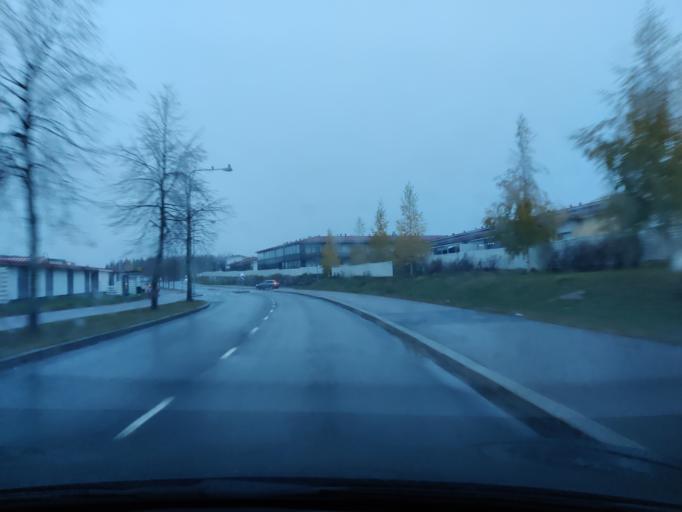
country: FI
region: Northern Savo
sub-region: Kuopio
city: Kuopio
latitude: 62.8278
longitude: 27.6787
